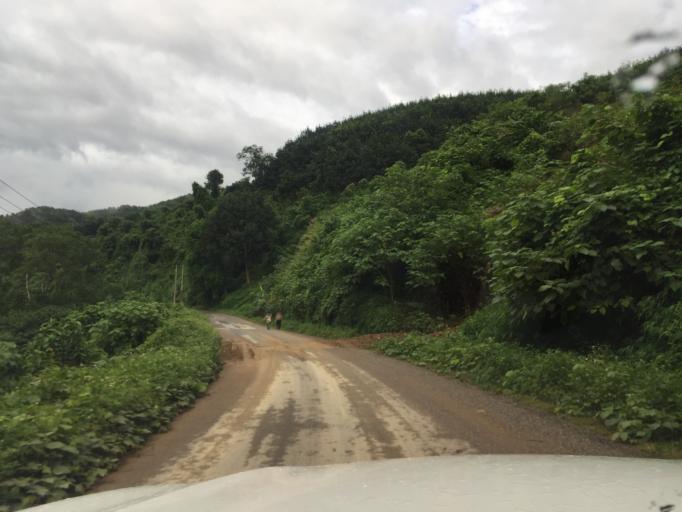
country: LA
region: Oudomxai
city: Muang La
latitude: 21.0222
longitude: 102.2329
